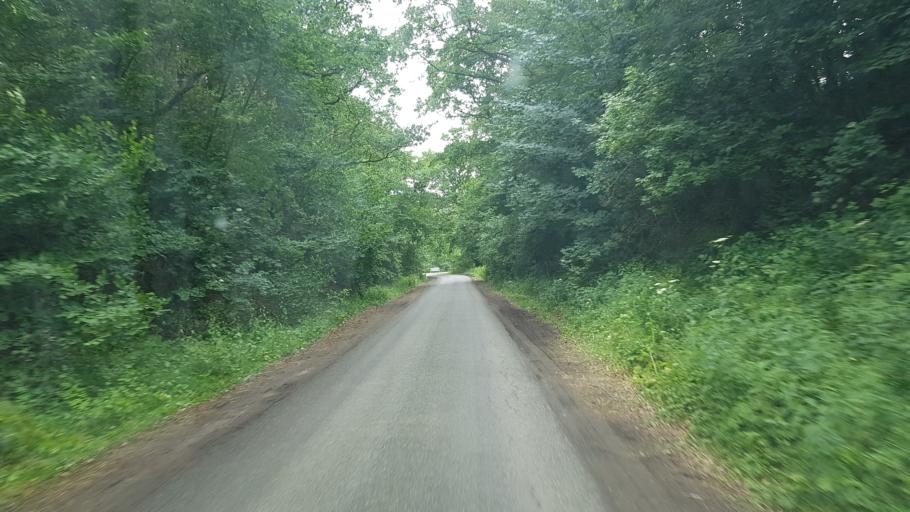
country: DK
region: South Denmark
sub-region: Kolding Kommune
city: Lunderskov
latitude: 55.5000
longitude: 9.3040
